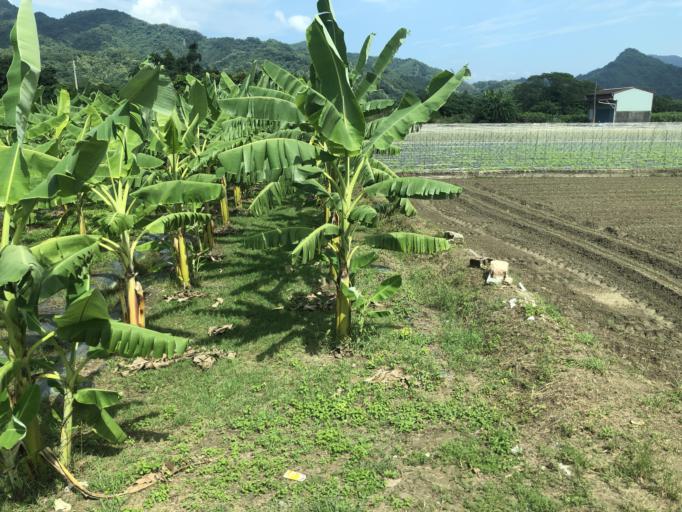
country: TW
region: Taiwan
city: Yujing
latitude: 22.9135
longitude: 120.5704
